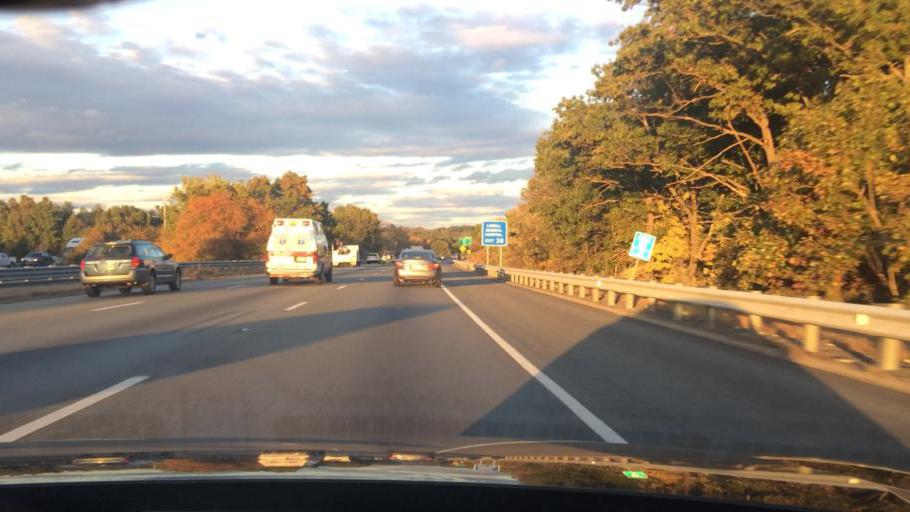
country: US
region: Massachusetts
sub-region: Middlesex County
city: Tewksbury
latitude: 42.6266
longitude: -71.2739
